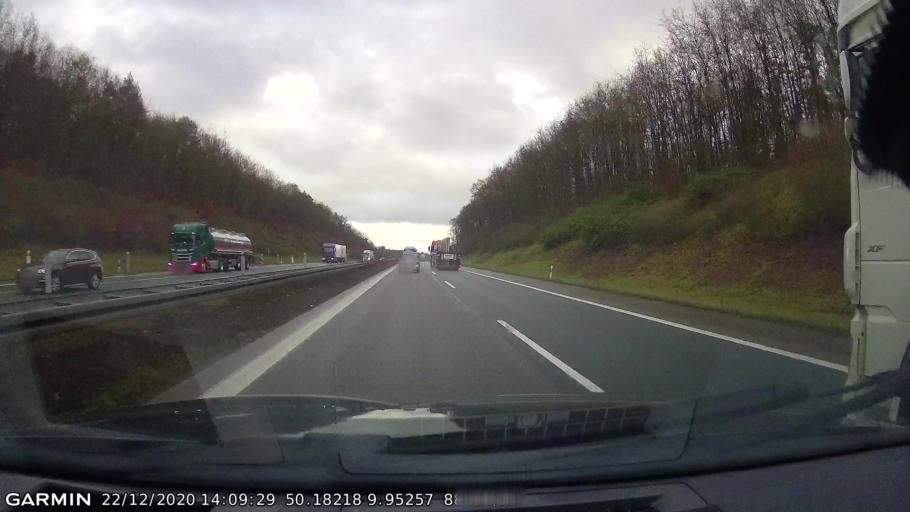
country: DE
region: Bavaria
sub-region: Regierungsbezirk Unterfranken
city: Oberthulba
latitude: 50.1822
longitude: 9.9526
